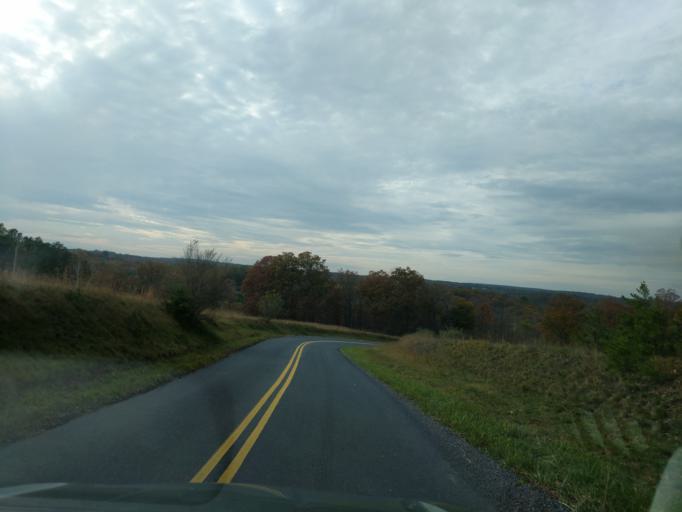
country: US
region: Virginia
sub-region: Frederick County
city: Shawnee Land
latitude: 39.3568
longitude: -78.2575
